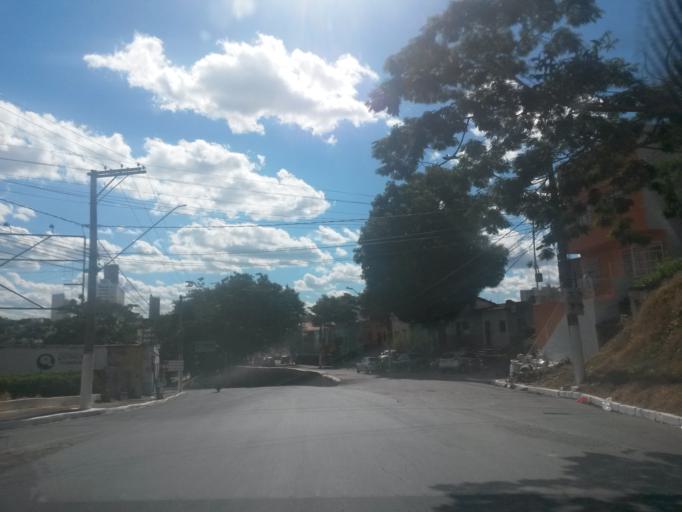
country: BR
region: Mato Grosso
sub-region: Cuiaba
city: Cuiaba
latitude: -15.5962
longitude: -56.0906
